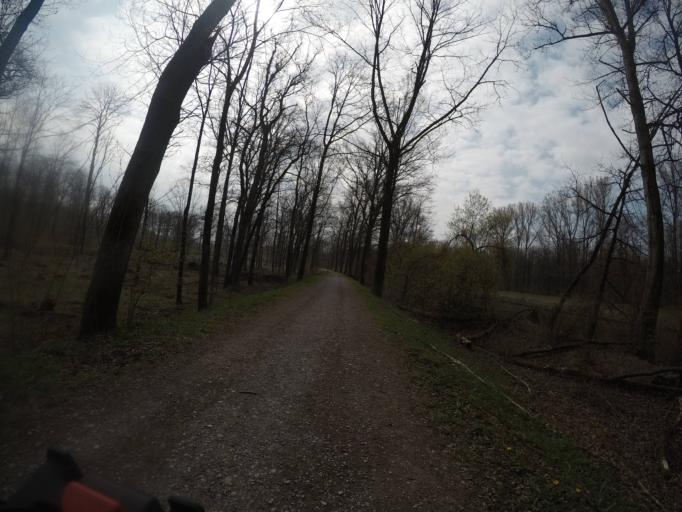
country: DE
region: Baden-Wuerttemberg
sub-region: Tuebingen Region
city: Ulm
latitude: 48.3751
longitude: 9.9719
